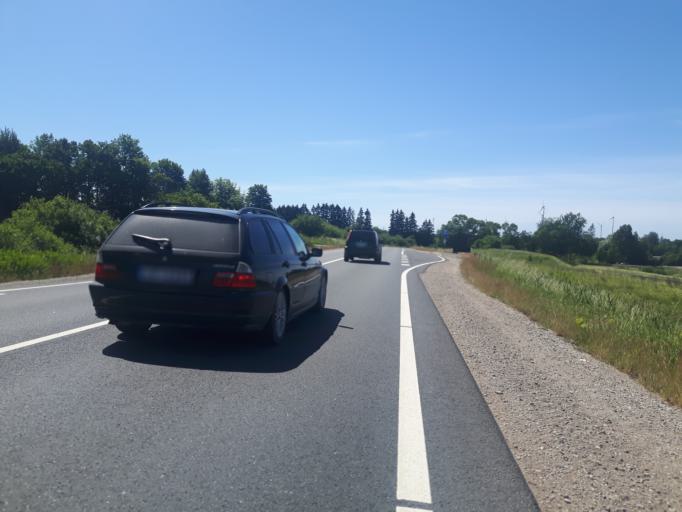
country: LV
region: Durbe
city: Liegi
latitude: 56.5579
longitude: 21.2607
